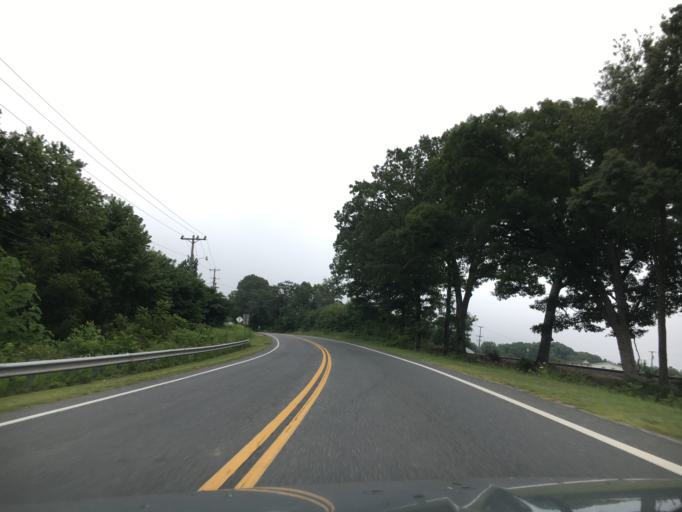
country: US
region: Virginia
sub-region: Campbell County
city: Brookneal
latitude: 37.0593
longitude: -78.9604
